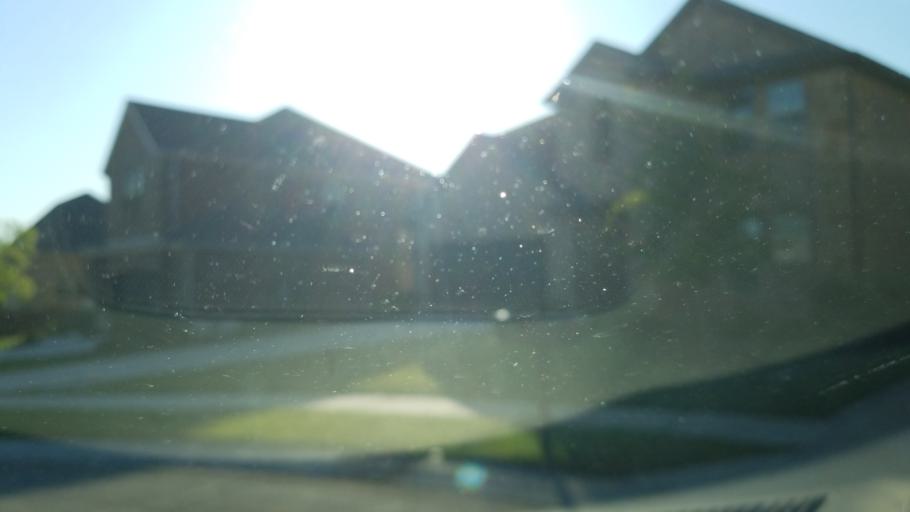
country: US
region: Texas
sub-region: Dallas County
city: Coppell
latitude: 32.9088
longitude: -96.9842
